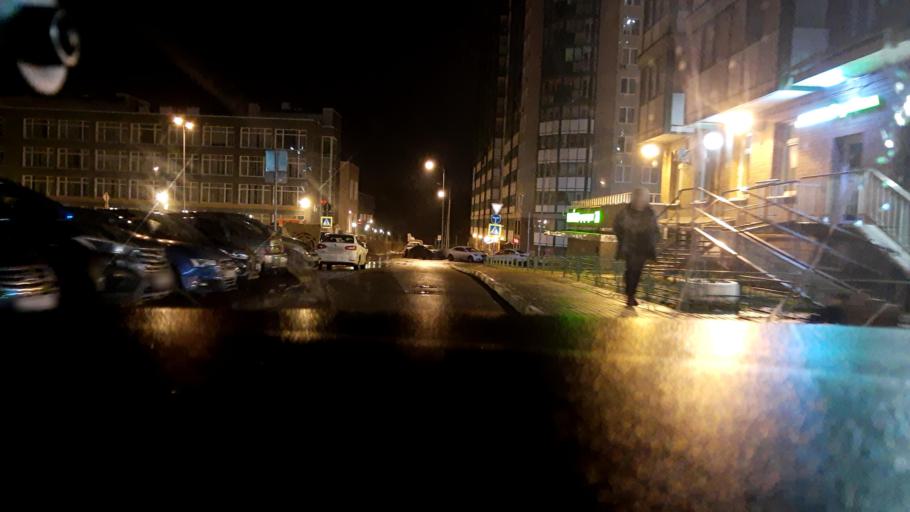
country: RU
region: Moskovskaya
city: Opalikha
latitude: 55.8351
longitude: 37.2809
